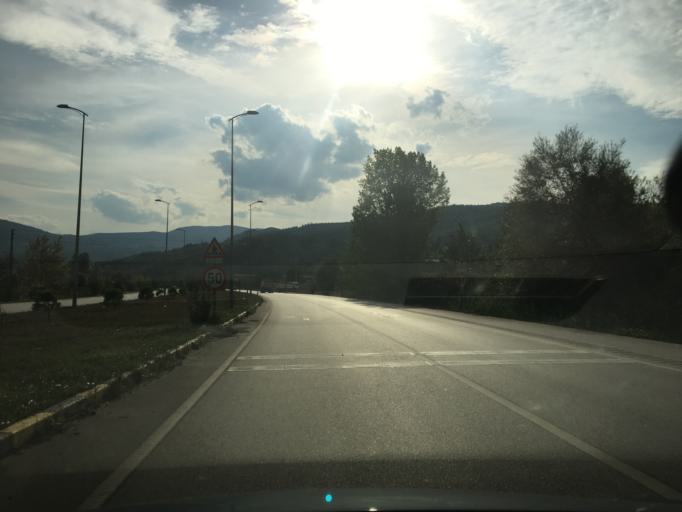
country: TR
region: Karabuk
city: Karabuk
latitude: 41.1205
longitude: 32.6765
